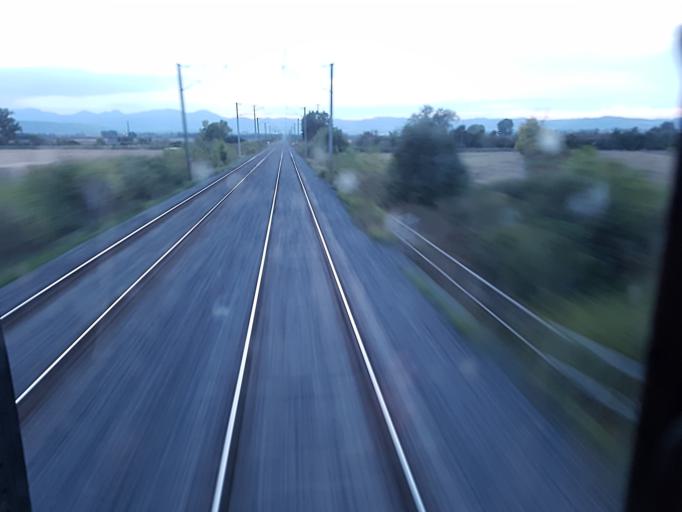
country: FR
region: Auvergne
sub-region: Departement du Puy-de-Dome
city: Ennezat
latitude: 45.9060
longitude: 3.1793
